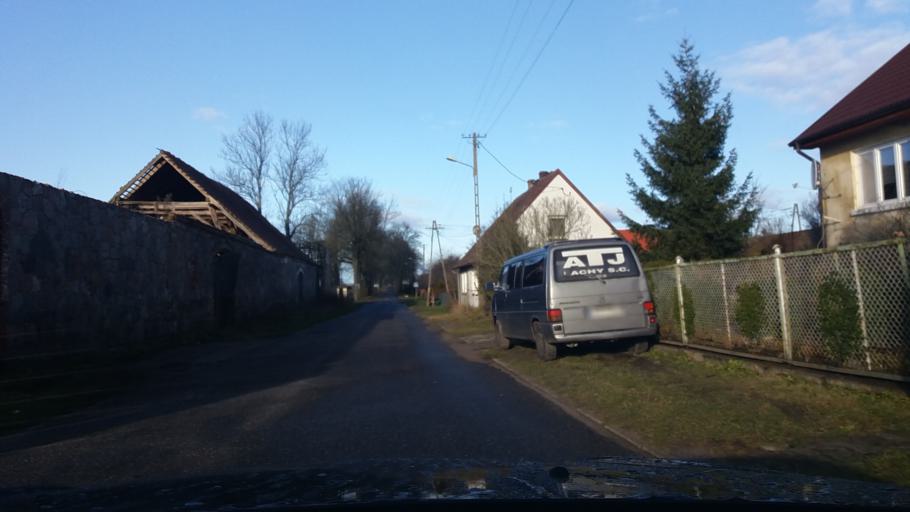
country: PL
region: West Pomeranian Voivodeship
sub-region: Powiat choszczenski
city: Drawno
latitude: 53.1934
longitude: 15.7882
